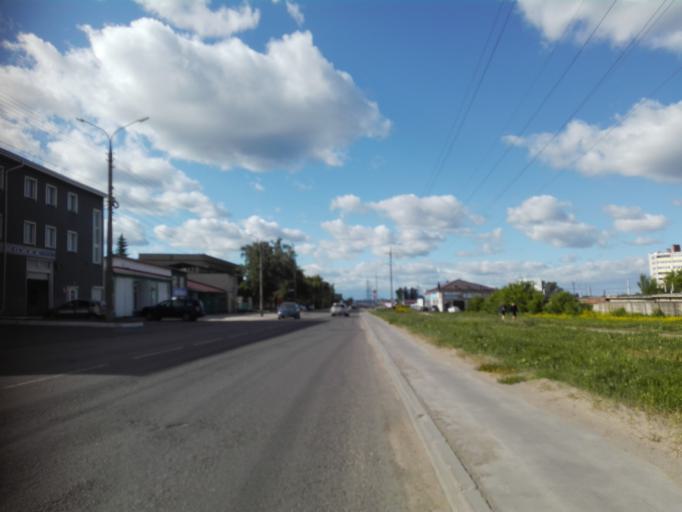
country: RU
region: Orjol
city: Orel
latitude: 52.9403
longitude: 36.0325
